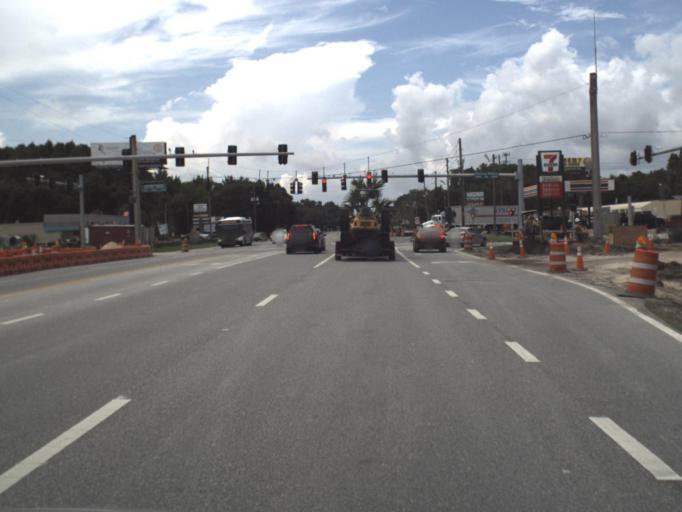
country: US
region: Florida
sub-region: Pasco County
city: Trinity
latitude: 28.1952
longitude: -82.6990
